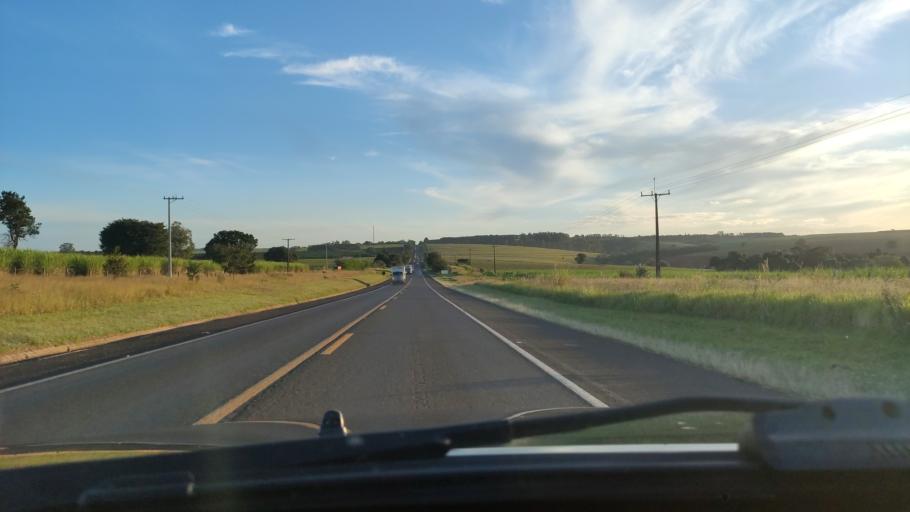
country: BR
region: Sao Paulo
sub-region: Avare
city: Avare
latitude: -23.0100
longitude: -48.8511
